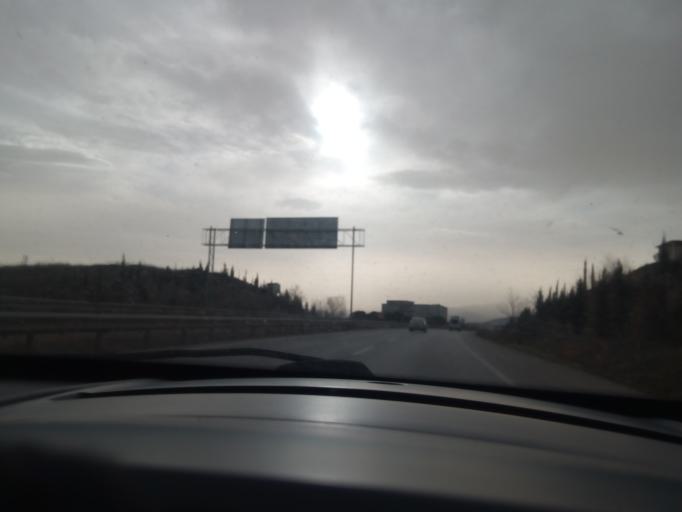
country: TR
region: Bursa
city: Tatkavakli
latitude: 40.0464
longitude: 28.3760
